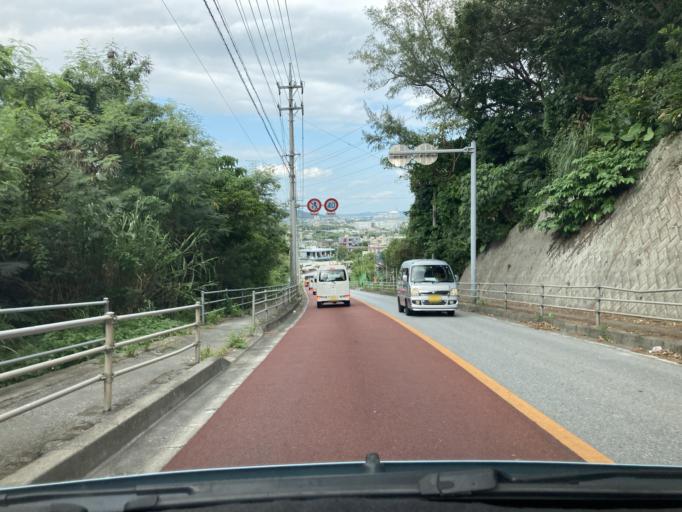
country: JP
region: Okinawa
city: Ginowan
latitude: 26.2529
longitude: 127.7822
